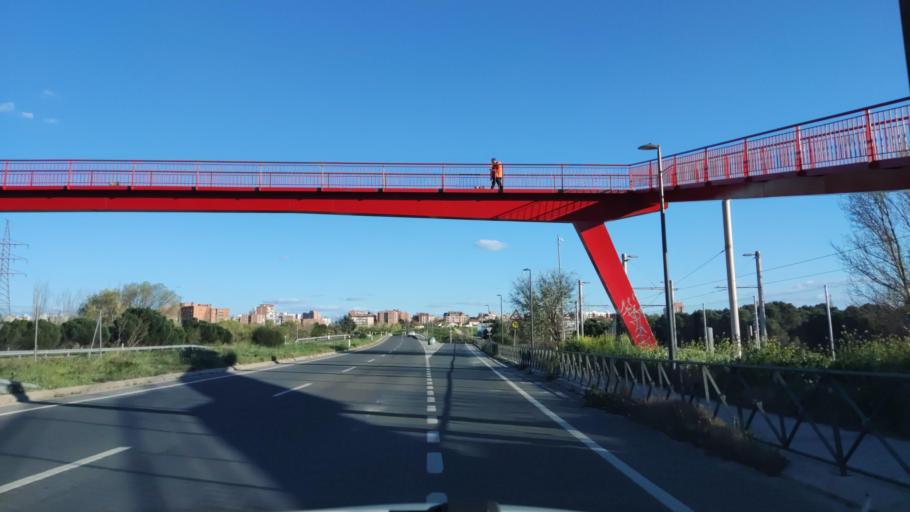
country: ES
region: Madrid
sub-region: Provincia de Madrid
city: Latina
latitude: 40.4024
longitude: -3.7811
